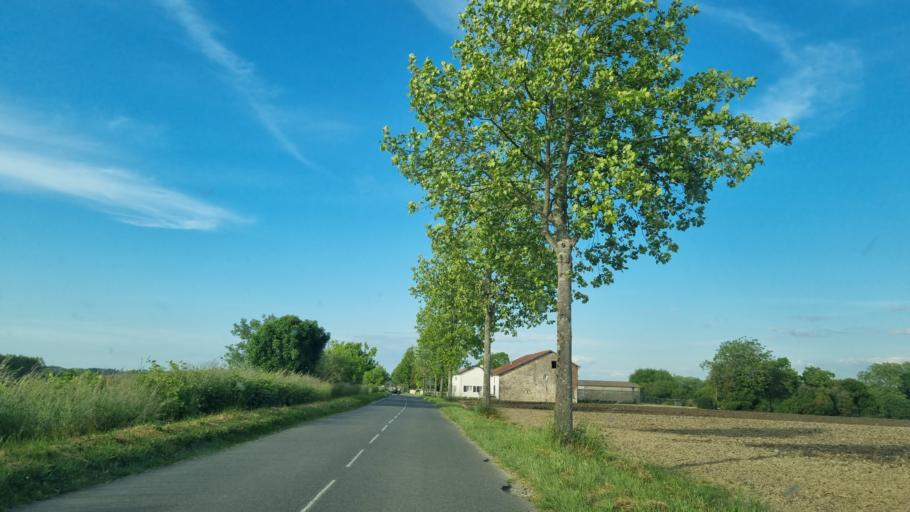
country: FR
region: Aquitaine
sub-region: Departement des Pyrenees-Atlantiques
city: Bardos
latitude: 43.5386
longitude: -1.2039
